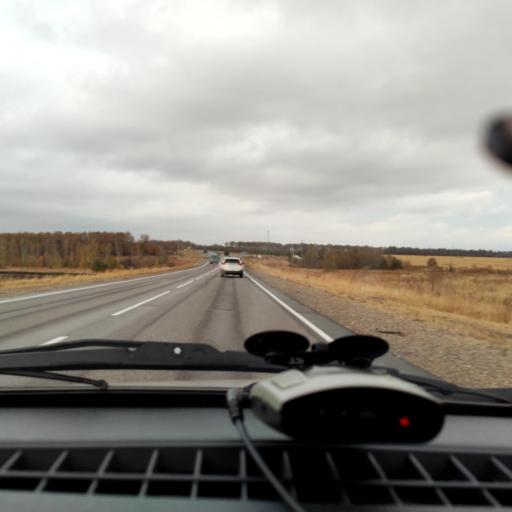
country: RU
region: Voronezj
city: Kolodeznyy
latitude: 51.3662
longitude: 39.0236
